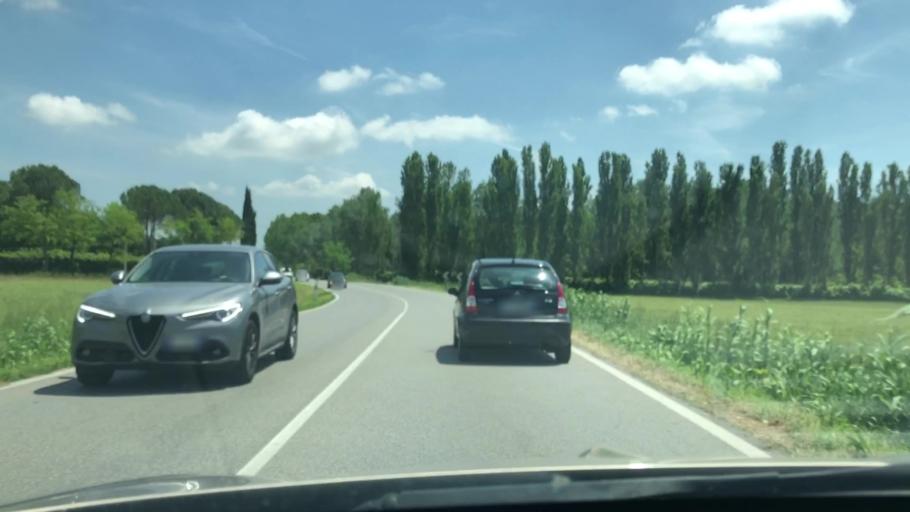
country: IT
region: Tuscany
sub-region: Province of Pisa
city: Treggiaia
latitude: 43.6158
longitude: 10.6778
